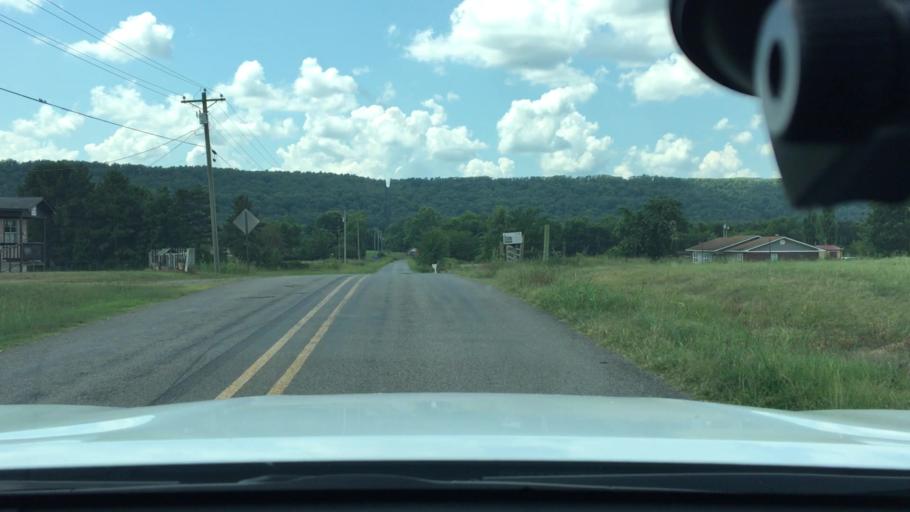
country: US
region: Arkansas
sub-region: Logan County
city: Paris
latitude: 35.2720
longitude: -93.6516
